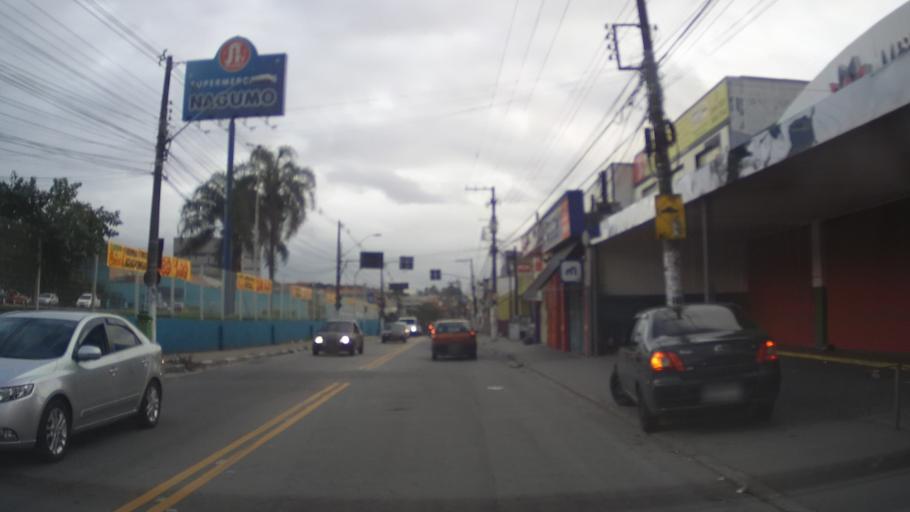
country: BR
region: Sao Paulo
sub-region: Itaquaquecetuba
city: Itaquaquecetuba
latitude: -23.4442
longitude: -46.4079
